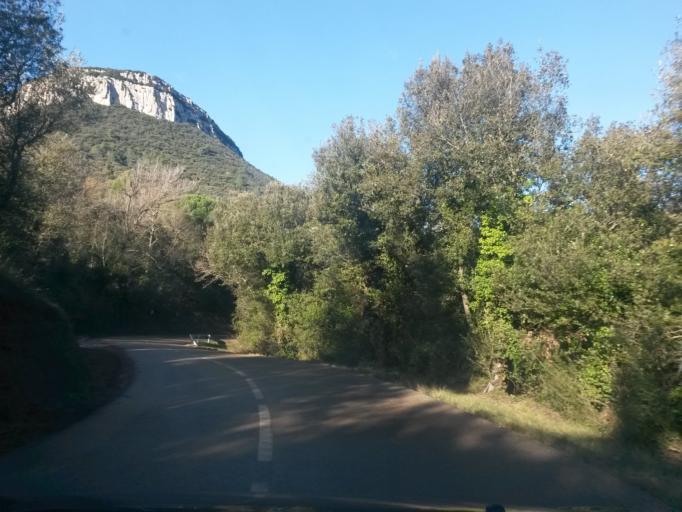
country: ES
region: Catalonia
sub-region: Provincia de Girona
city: la Cellera de Ter
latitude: 42.0158
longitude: 2.6700
